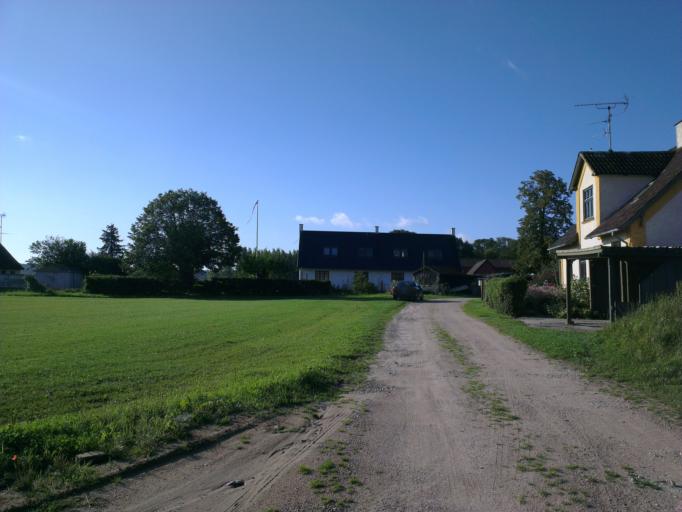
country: DK
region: Capital Region
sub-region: Frederikssund Kommune
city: Jaegerspris
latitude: 55.8667
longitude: 11.9897
